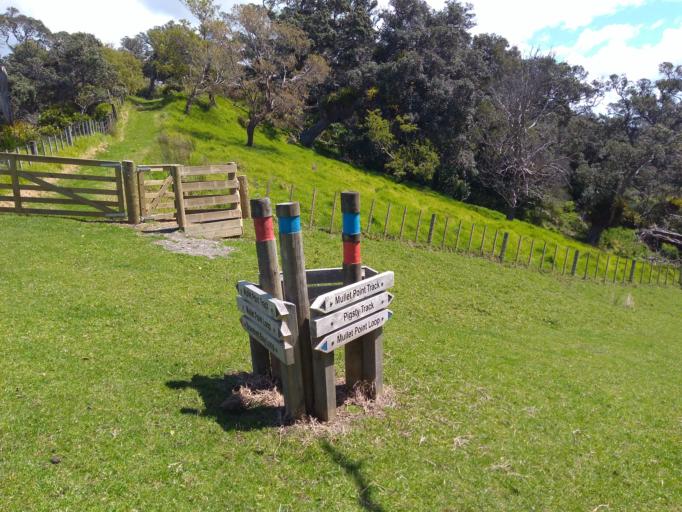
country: NZ
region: Auckland
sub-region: Auckland
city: Warkworth
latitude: -36.4443
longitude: 174.7747
